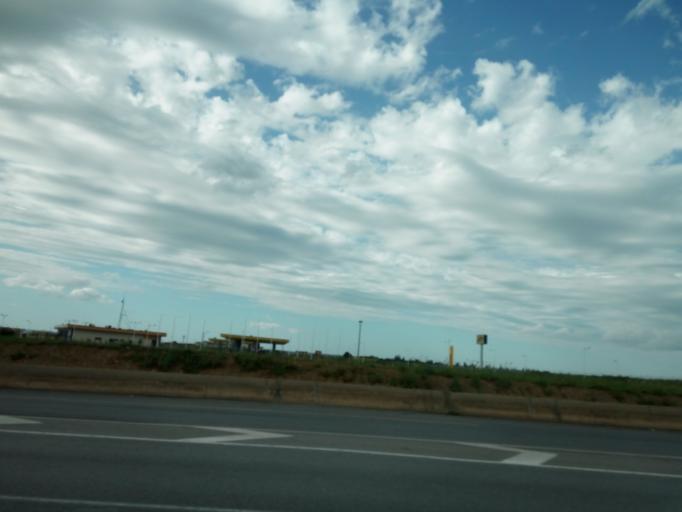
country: DZ
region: Tipaza
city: Mouzaia
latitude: 36.4494
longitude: 2.6599
